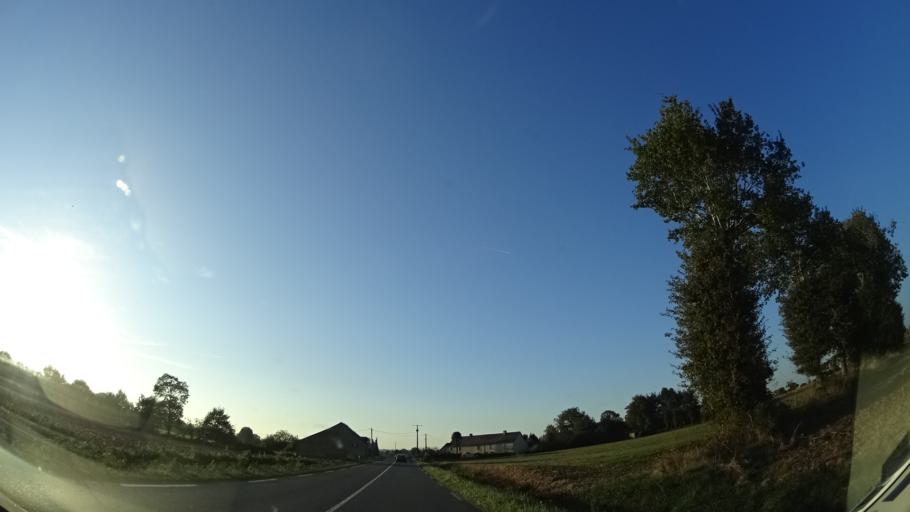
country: FR
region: Brittany
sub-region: Departement d'Ille-et-Vilaine
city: La Meziere
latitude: 48.2106
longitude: -1.7616
